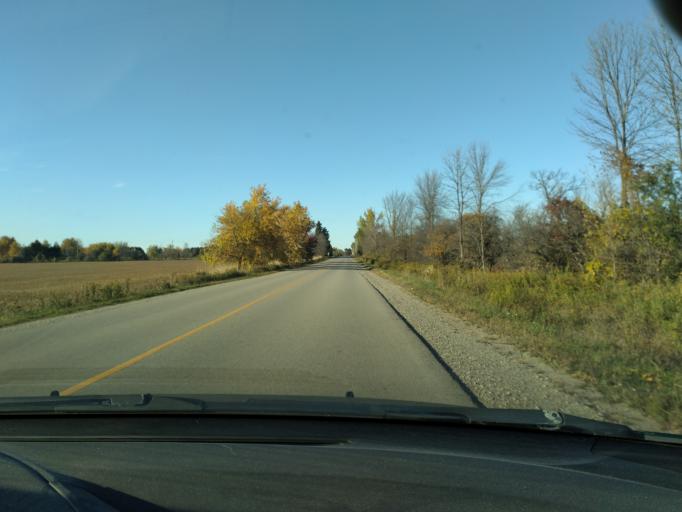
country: CA
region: Ontario
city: Bradford West Gwillimbury
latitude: 44.0111
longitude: -79.7242
